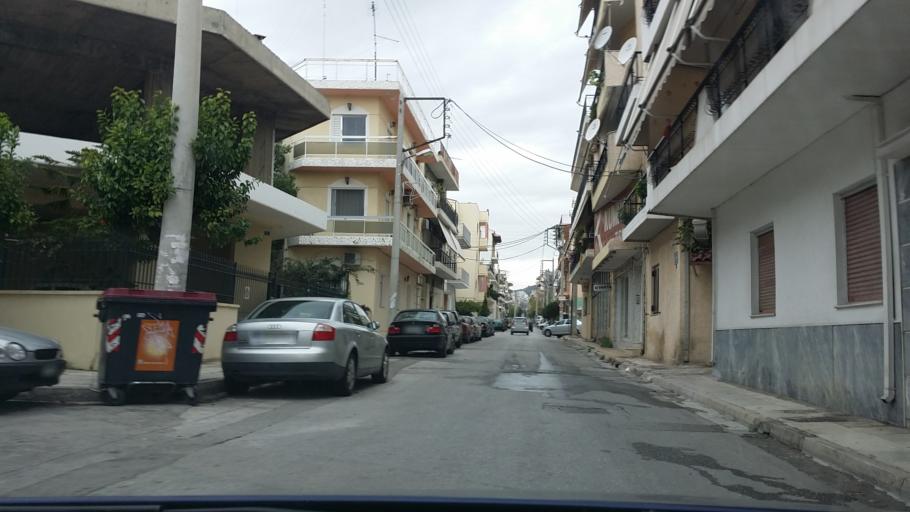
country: GR
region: Attica
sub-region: Nomarchia Athinas
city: Peristeri
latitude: 38.0242
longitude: 23.6928
